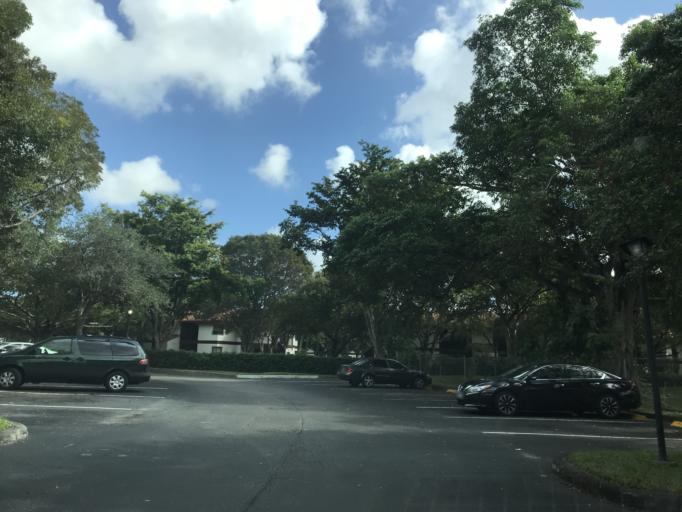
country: US
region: Florida
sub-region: Broward County
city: Coconut Creek
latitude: 26.2715
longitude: -80.1892
